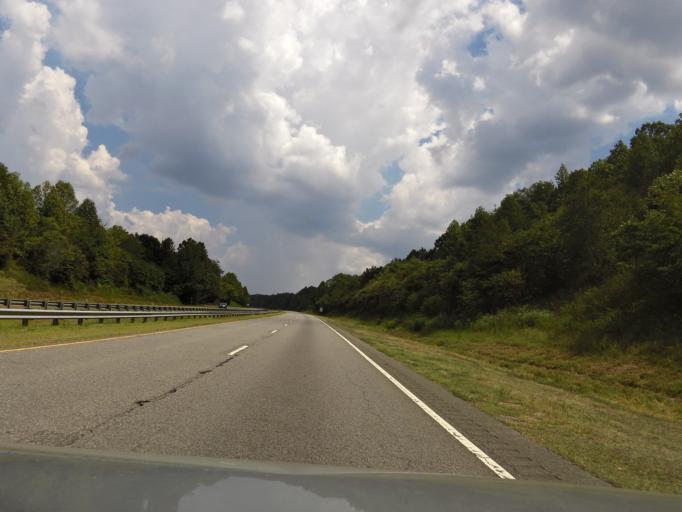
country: US
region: North Carolina
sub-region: Rutherford County
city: Rutherfordton
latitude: 35.2923
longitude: -81.9892
